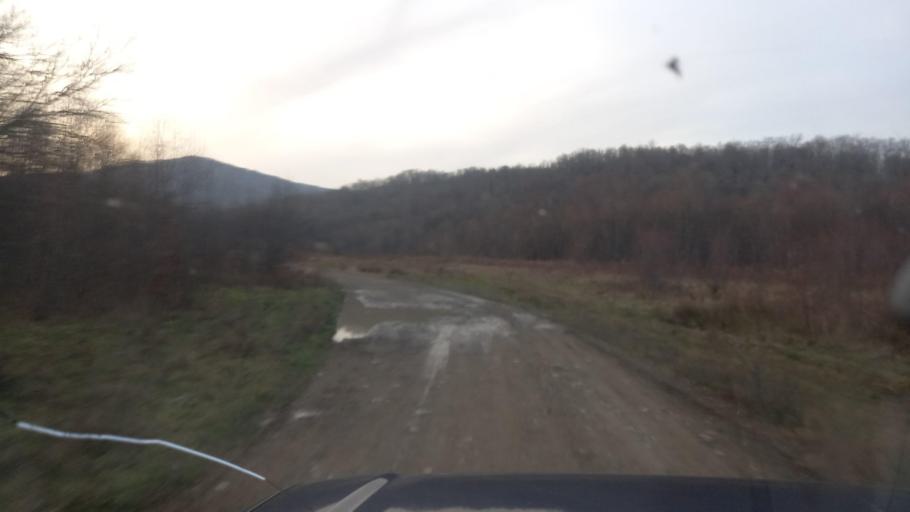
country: RU
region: Krasnodarskiy
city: Goryachiy Klyuch
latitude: 44.3819
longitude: 39.1537
